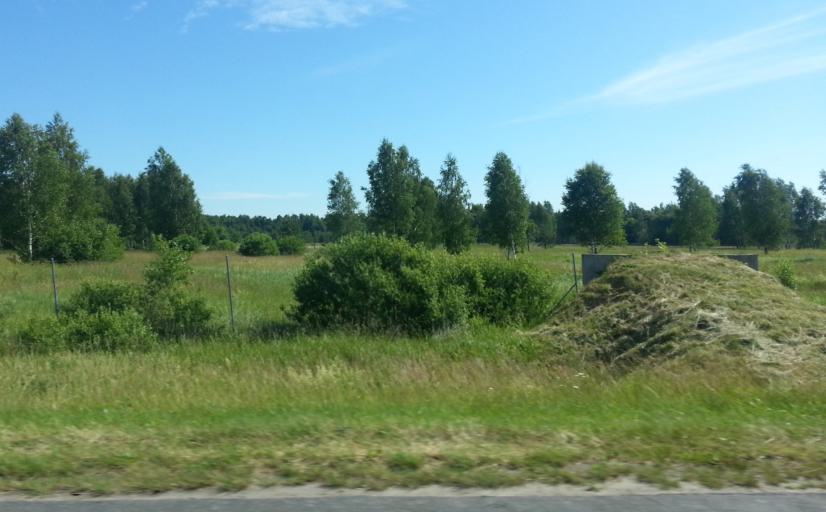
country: LT
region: Vilnius County
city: Ukmerge
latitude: 55.4876
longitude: 24.6320
